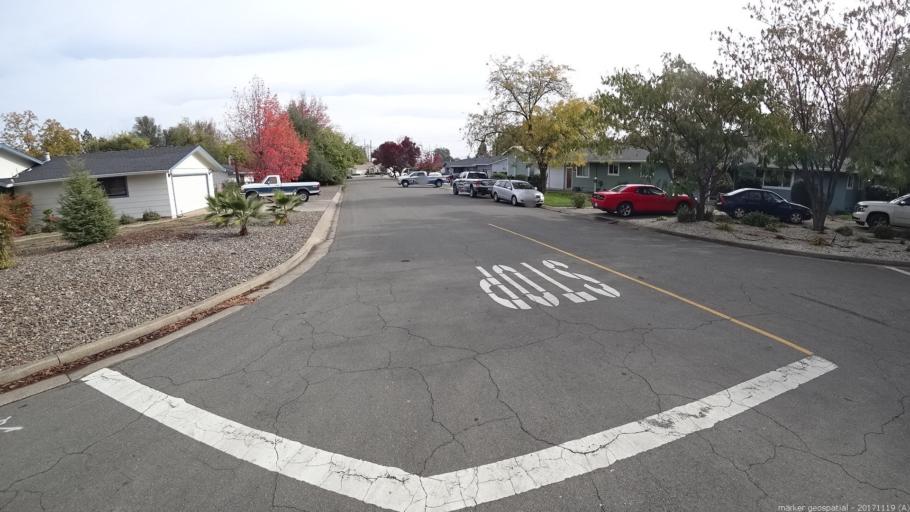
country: US
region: California
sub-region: Shasta County
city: Anderson
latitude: 40.4876
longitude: -122.3082
